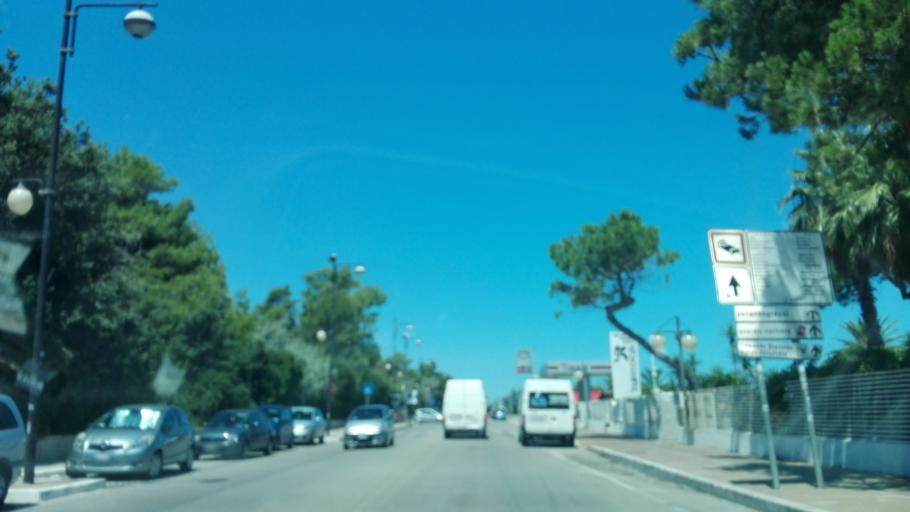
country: IT
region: Abruzzo
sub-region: Provincia di Pescara
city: Villa Raspa
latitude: 42.4938
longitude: 14.1849
